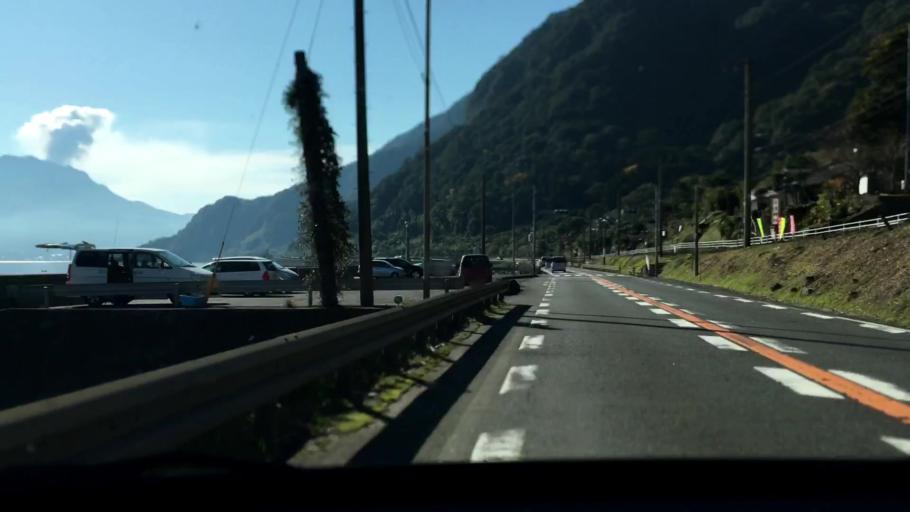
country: JP
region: Kagoshima
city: Kajiki
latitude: 31.6830
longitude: 130.6096
